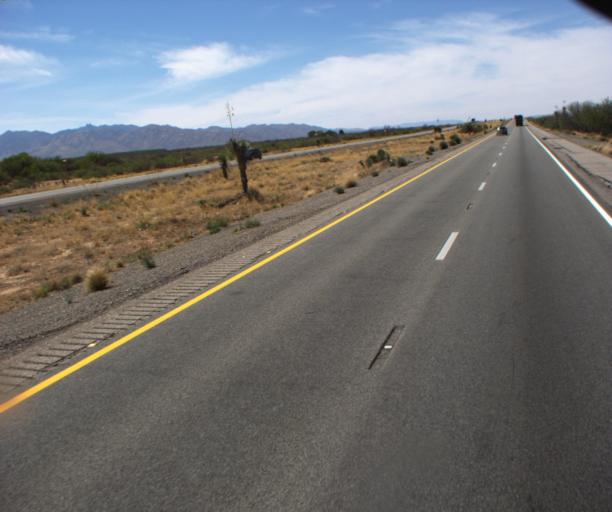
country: US
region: Arizona
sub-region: Cochise County
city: Willcox
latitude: 32.3055
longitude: -109.3890
